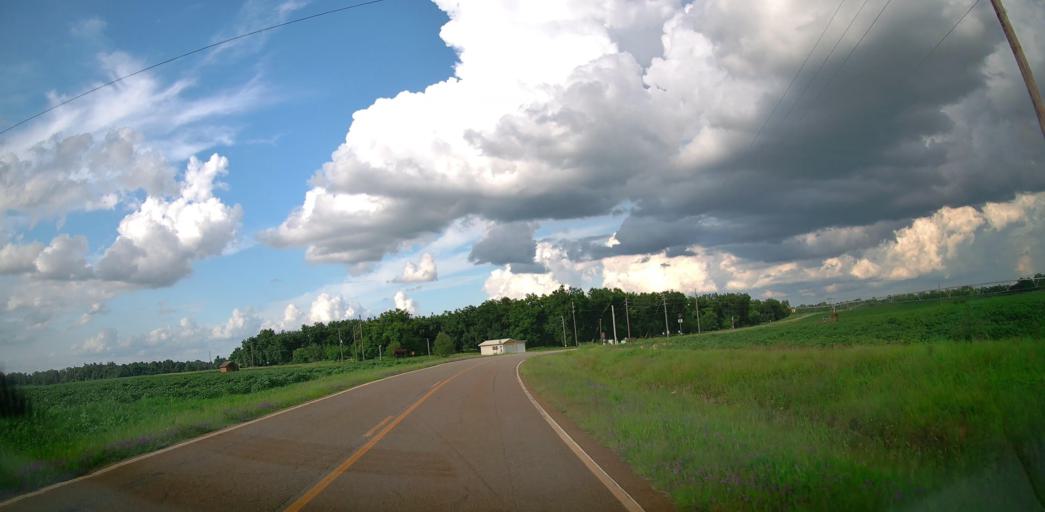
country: US
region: Georgia
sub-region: Bleckley County
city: Cochran
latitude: 32.4100
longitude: -83.4017
